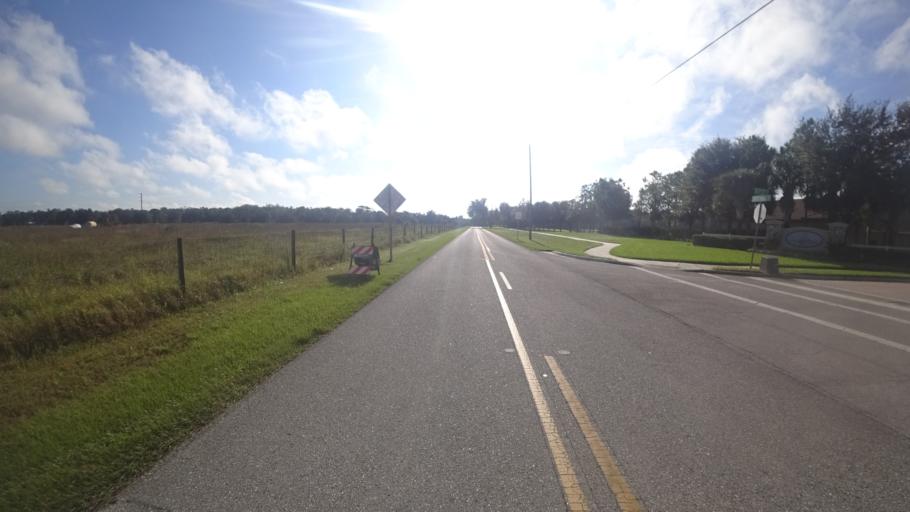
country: US
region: Florida
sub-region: Manatee County
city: Ellenton
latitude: 27.5644
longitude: -82.4082
